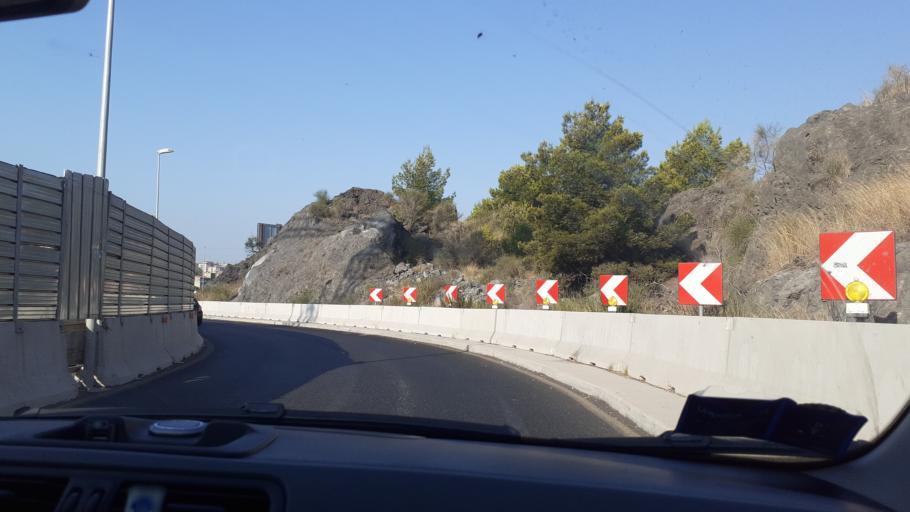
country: IT
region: Sicily
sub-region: Catania
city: Misterbianco
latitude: 37.5144
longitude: 15.0425
